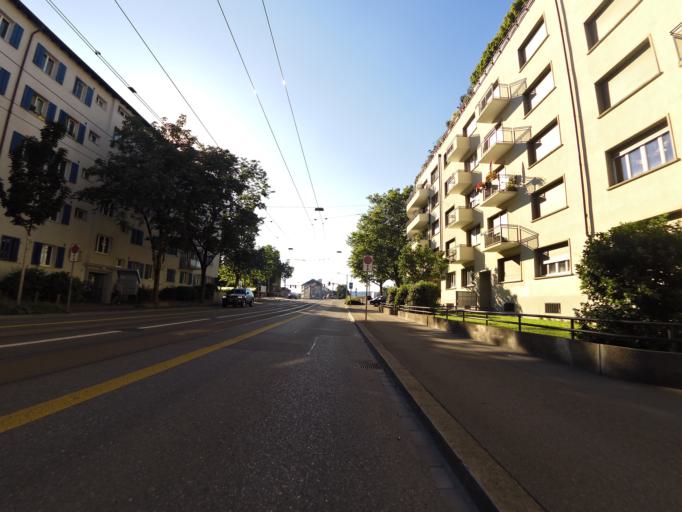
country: CH
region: Zurich
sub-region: Bezirk Zuerich
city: Aussersihl
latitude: 47.3793
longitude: 8.5221
